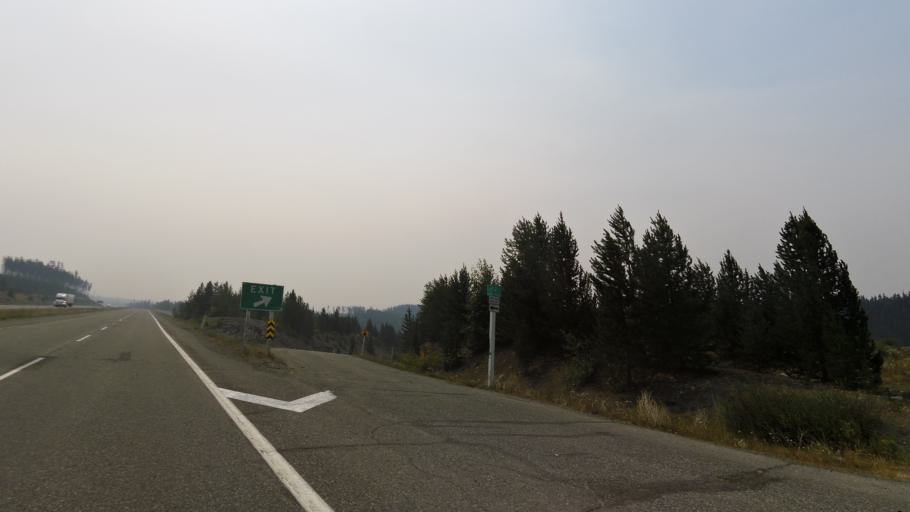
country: CA
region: British Columbia
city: Princeton
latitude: 49.8752
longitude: -120.3111
